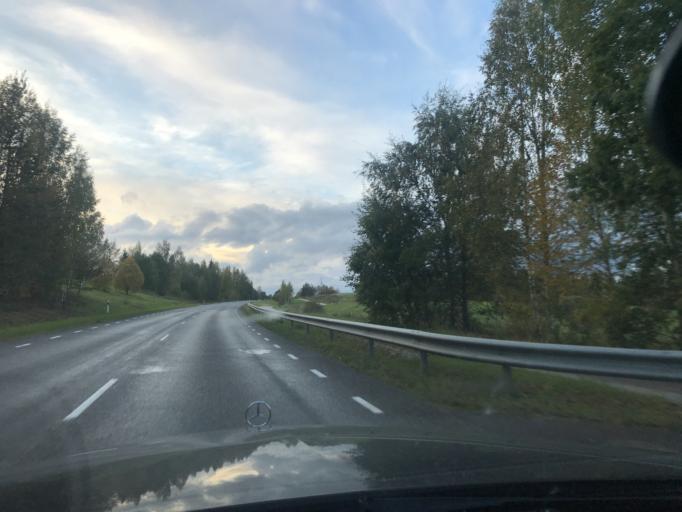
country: EE
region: Vorumaa
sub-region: Antsla vald
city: Vana-Antsla
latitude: 57.9276
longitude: 26.3275
